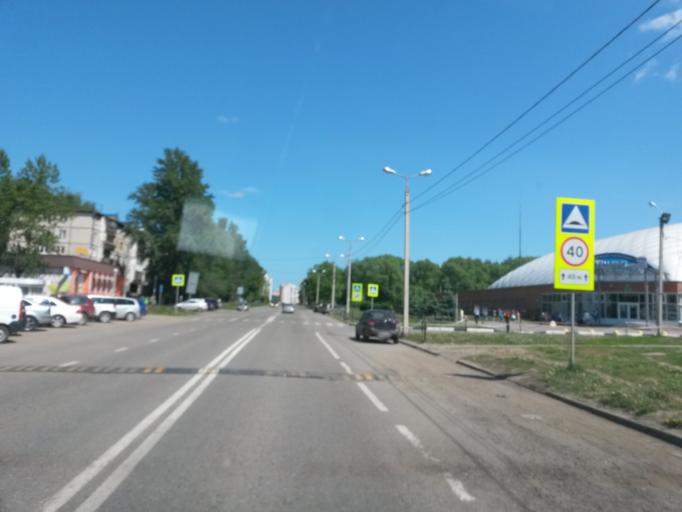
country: RU
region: Jaroslavl
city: Yaroslavl
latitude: 57.6879
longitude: 39.7696
